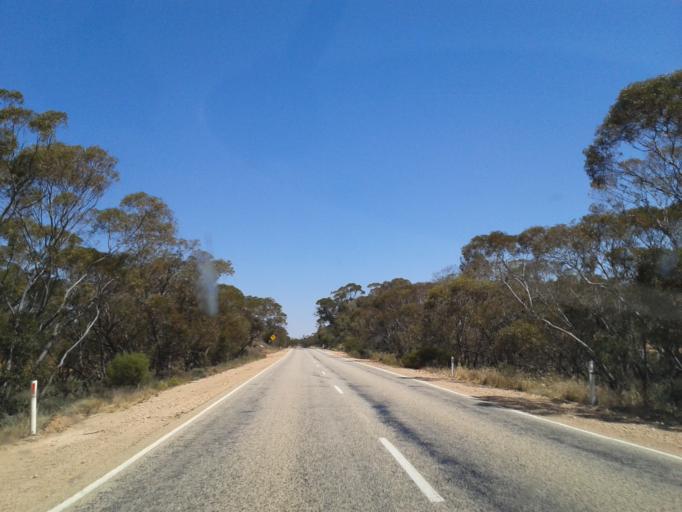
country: AU
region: Victoria
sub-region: Swan Hill
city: Swan Hill
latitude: -34.8376
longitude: 143.2617
